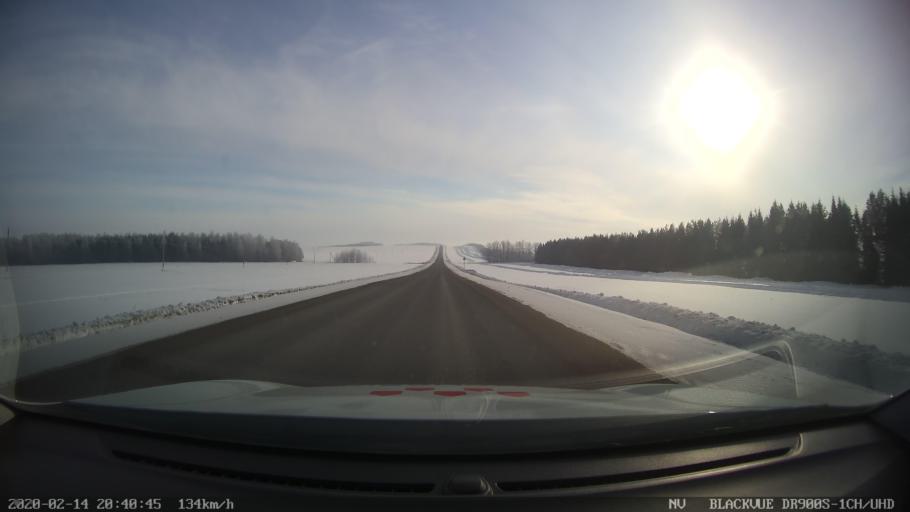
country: RU
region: Tatarstan
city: Kuybyshevskiy Zaton
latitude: 55.3371
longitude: 49.0996
